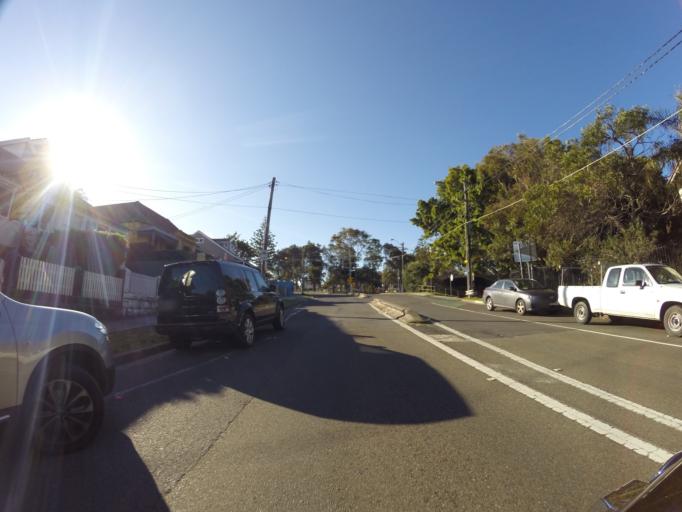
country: AU
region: New South Wales
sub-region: Randwick
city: Clovelly
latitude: -33.9069
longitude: 151.2597
